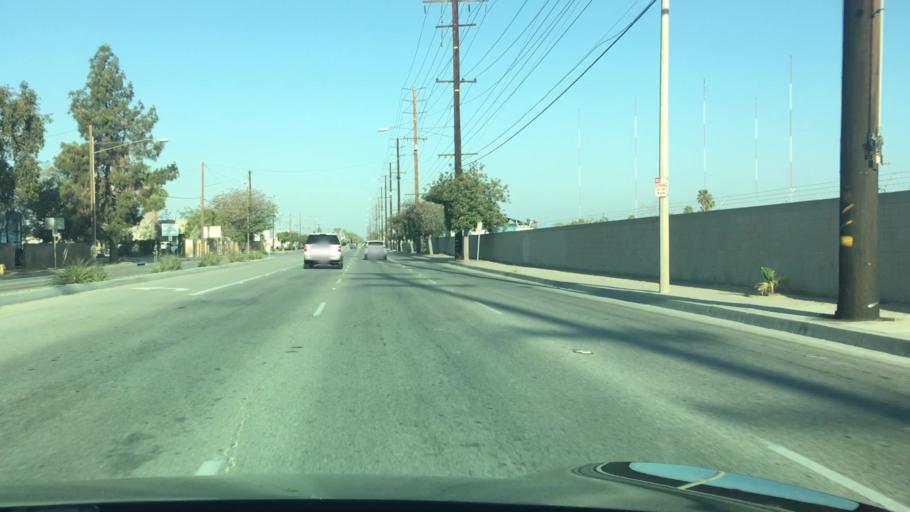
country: US
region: California
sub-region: Los Angeles County
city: Mayflower Village
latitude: 34.1130
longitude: -117.9922
